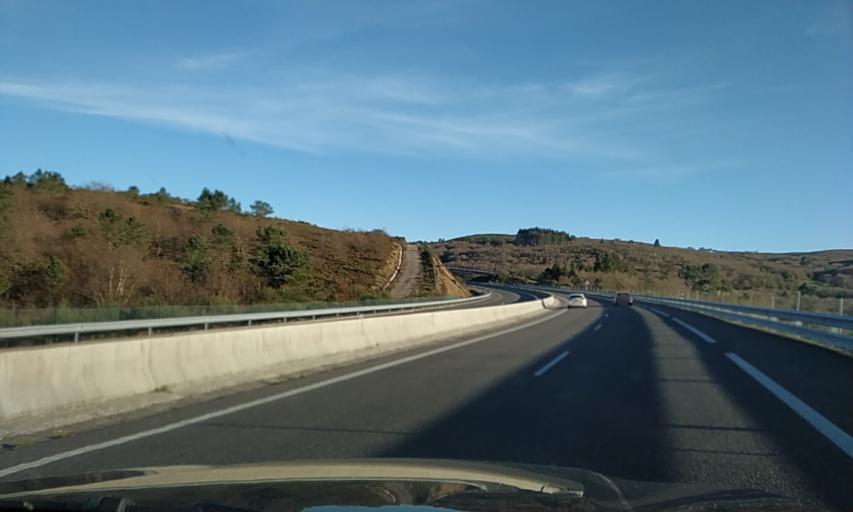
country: ES
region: Galicia
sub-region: Provincia de Pontevedra
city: Dozon
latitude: 42.5709
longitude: -8.0602
